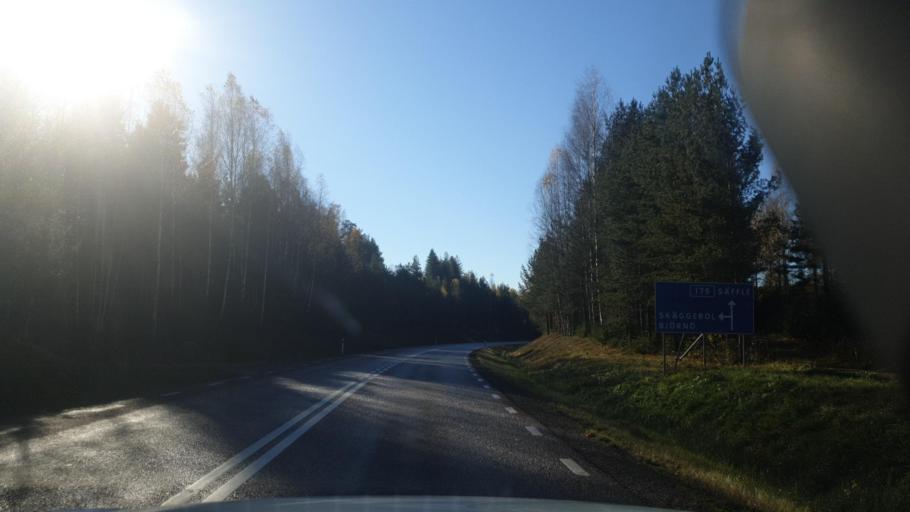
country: SE
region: Vaermland
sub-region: Arvika Kommun
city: Arvika
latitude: 59.4629
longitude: 12.7744
